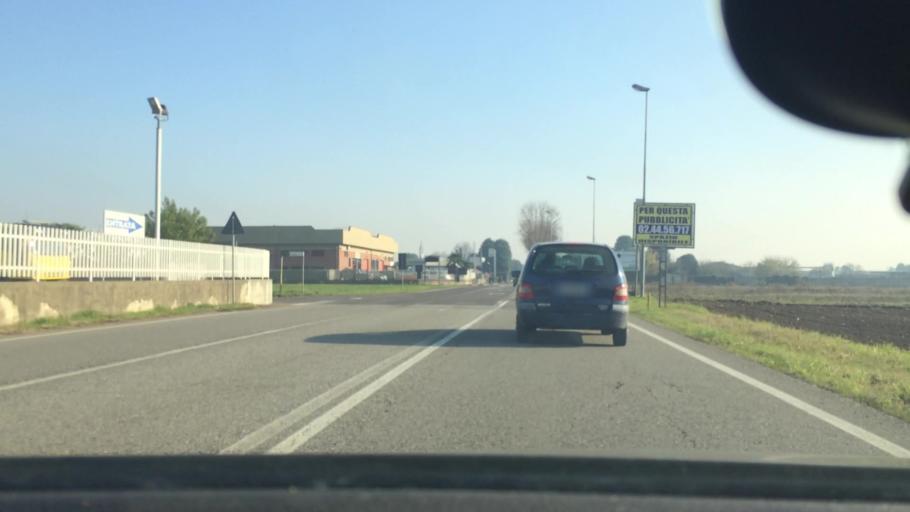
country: IT
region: Lombardy
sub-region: Provincia di Como
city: Turate
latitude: 45.6538
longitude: 9.0211
